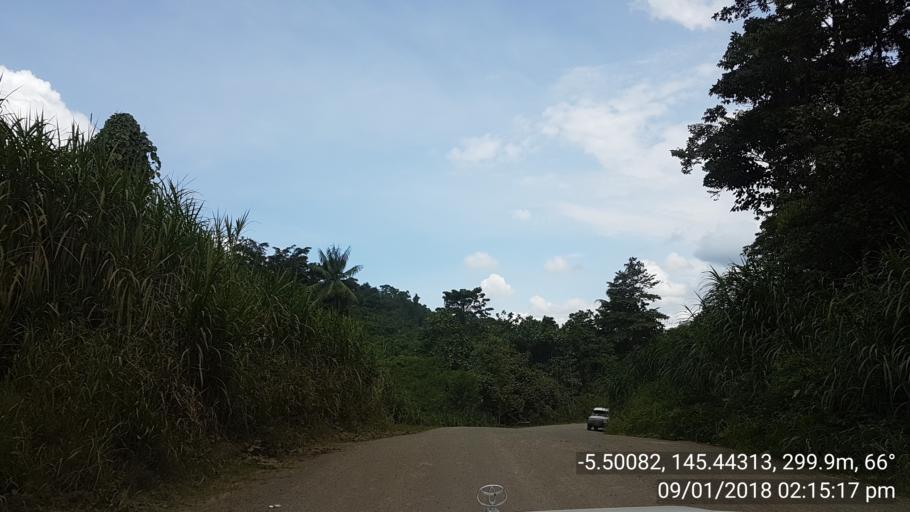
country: PG
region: Madang
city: Madang
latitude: -5.5007
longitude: 145.4432
